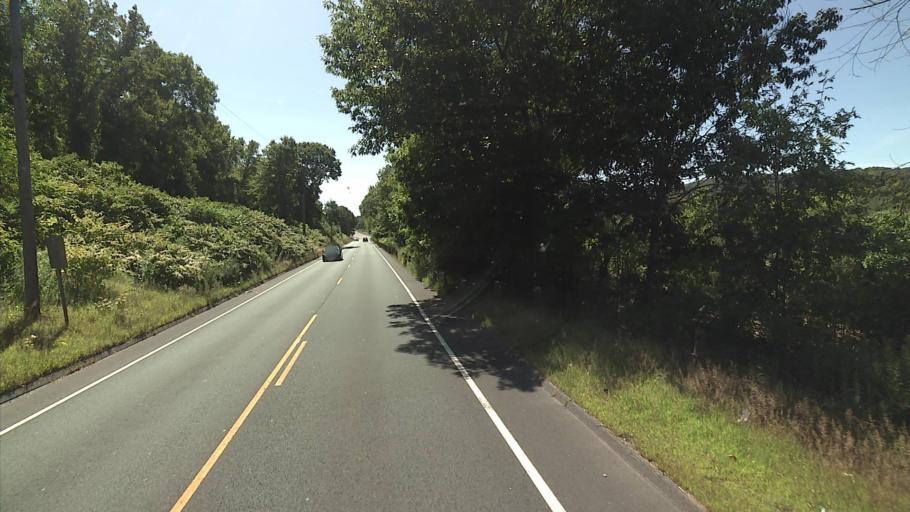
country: US
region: Connecticut
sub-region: New Haven County
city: Waterbury
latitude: 41.5725
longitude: -73.0527
